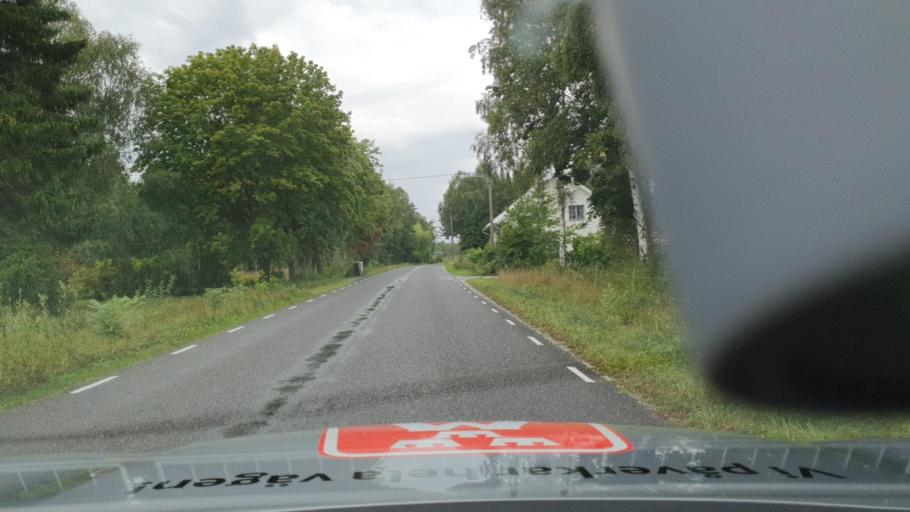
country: SE
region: Gotland
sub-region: Gotland
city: Visby
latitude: 57.5741
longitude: 18.4923
